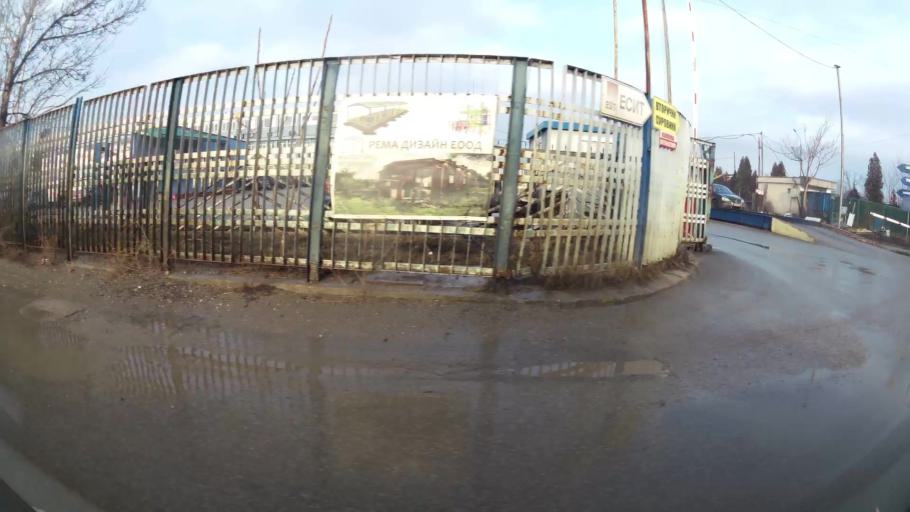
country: BG
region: Sofia-Capital
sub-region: Stolichna Obshtina
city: Sofia
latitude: 42.7406
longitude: 23.3281
